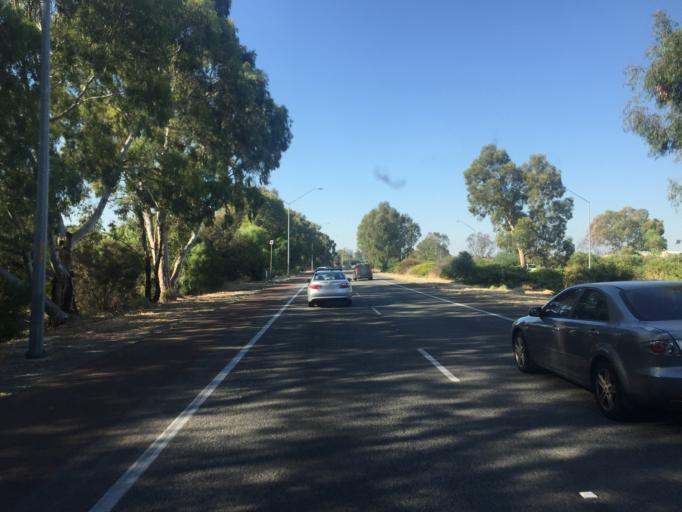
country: AU
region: Western Australia
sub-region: Canning
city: East Cannington
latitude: -32.0160
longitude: 115.9717
